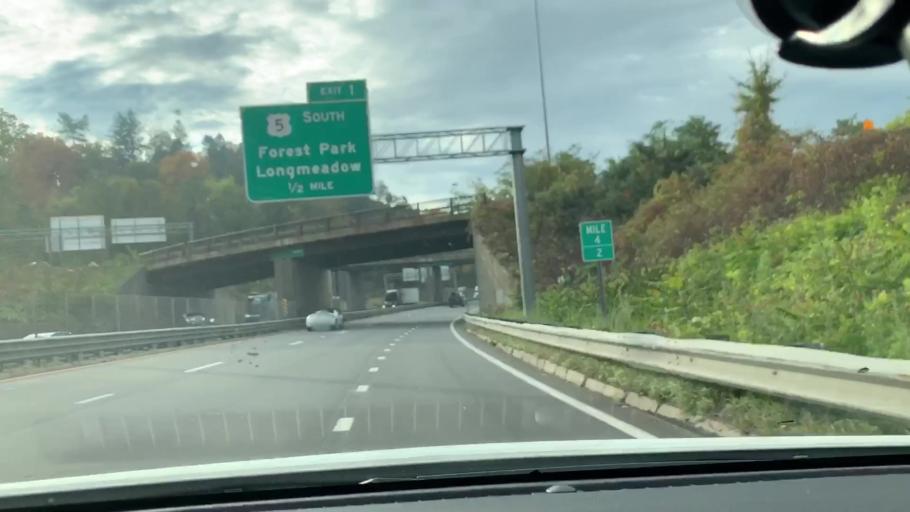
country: US
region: Massachusetts
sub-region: Hampden County
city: Springfield
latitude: 42.0831
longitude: -72.5793
